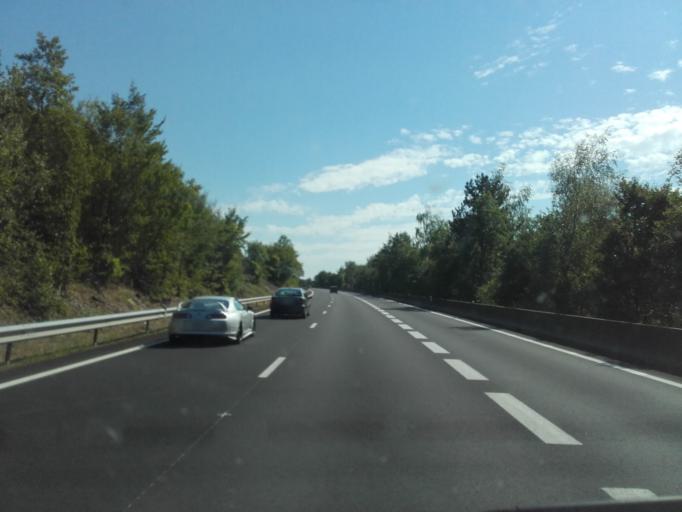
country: FR
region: Bourgogne
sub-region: Departement de la Cote-d'Or
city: Savigny-les-Beaune
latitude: 47.1334
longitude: 4.6991
